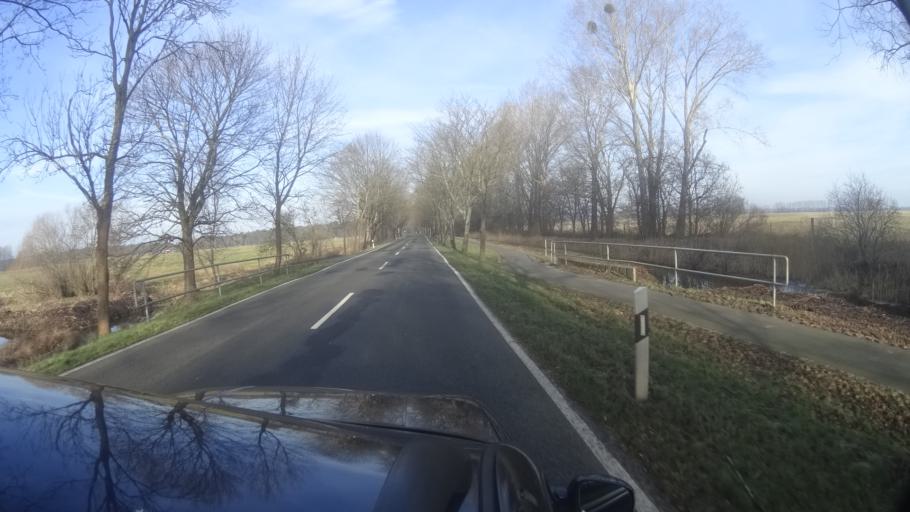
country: DE
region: Brandenburg
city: Kremmen
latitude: 52.7813
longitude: 13.0453
